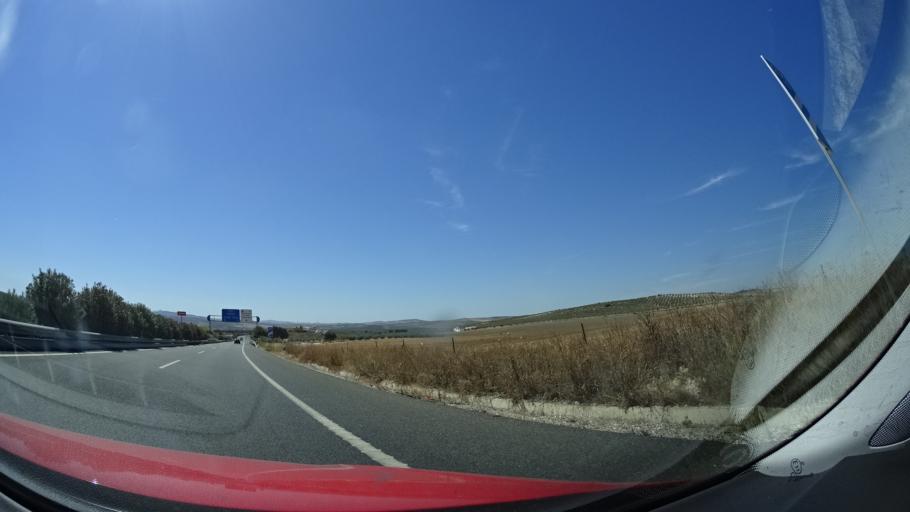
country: ES
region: Andalusia
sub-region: Provincia de Sevilla
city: Aguadulce
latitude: 37.2671
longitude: -4.9549
